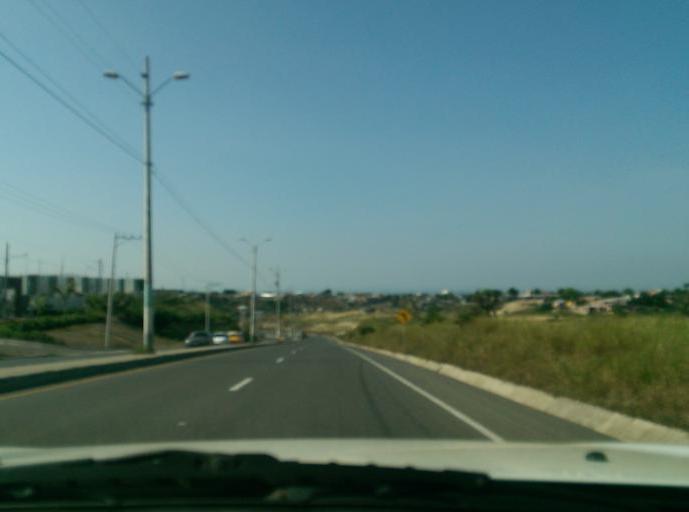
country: EC
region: Manabi
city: Manta
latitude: -0.9870
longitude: -80.7160
